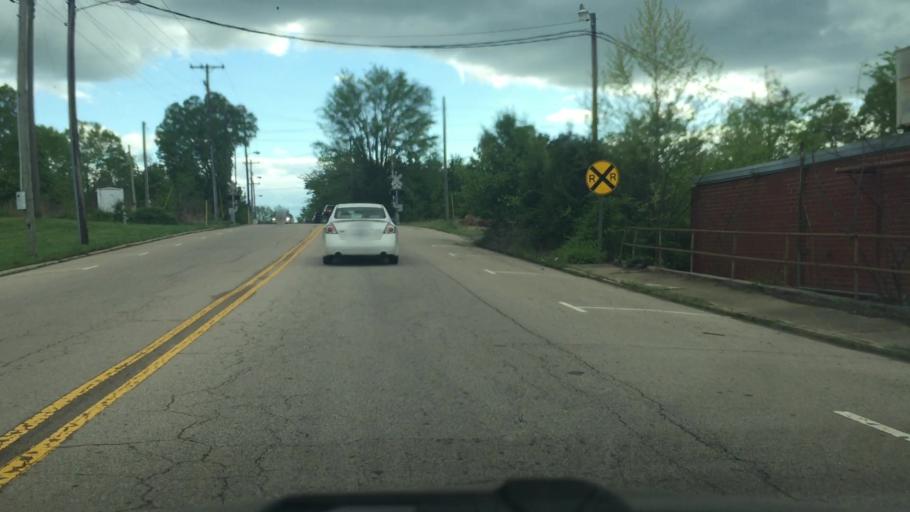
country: US
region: North Carolina
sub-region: Rowan County
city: Salisbury
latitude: 35.6795
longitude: -80.4881
